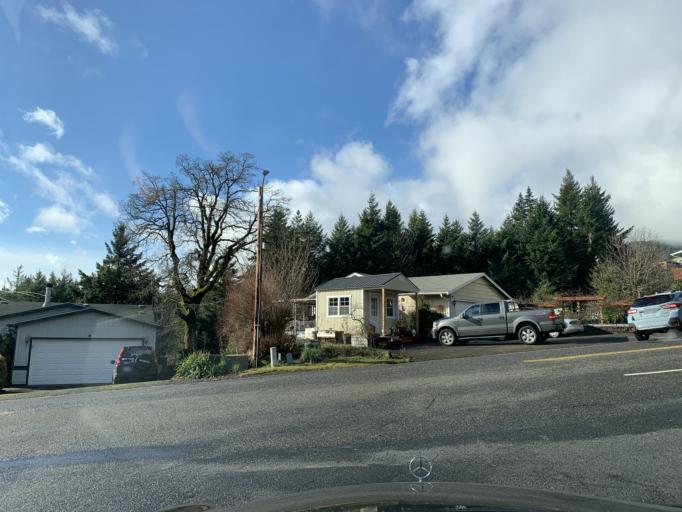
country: US
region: Washington
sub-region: Skamania County
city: Carson
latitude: 45.7201
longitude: -121.8173
